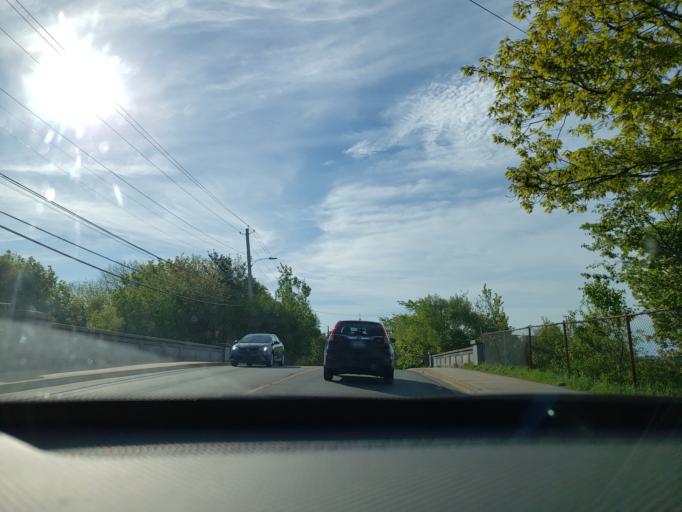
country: CA
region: Nova Scotia
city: Halifax
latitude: 44.6493
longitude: -63.6235
